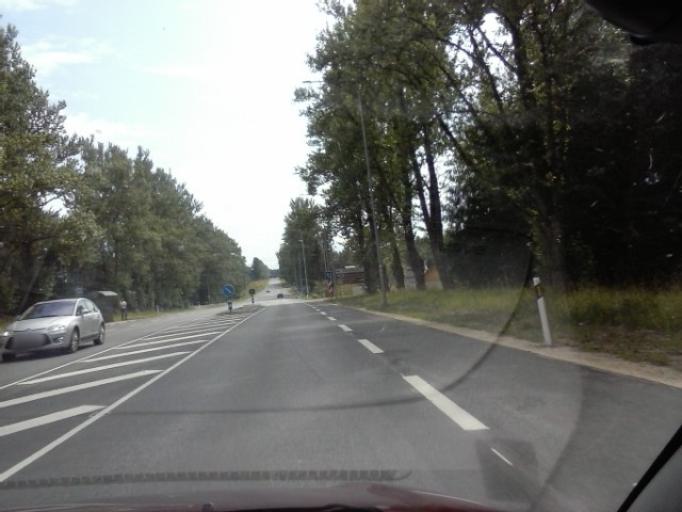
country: EE
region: Polvamaa
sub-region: Polva linn
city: Polva
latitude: 58.2840
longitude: 27.0019
